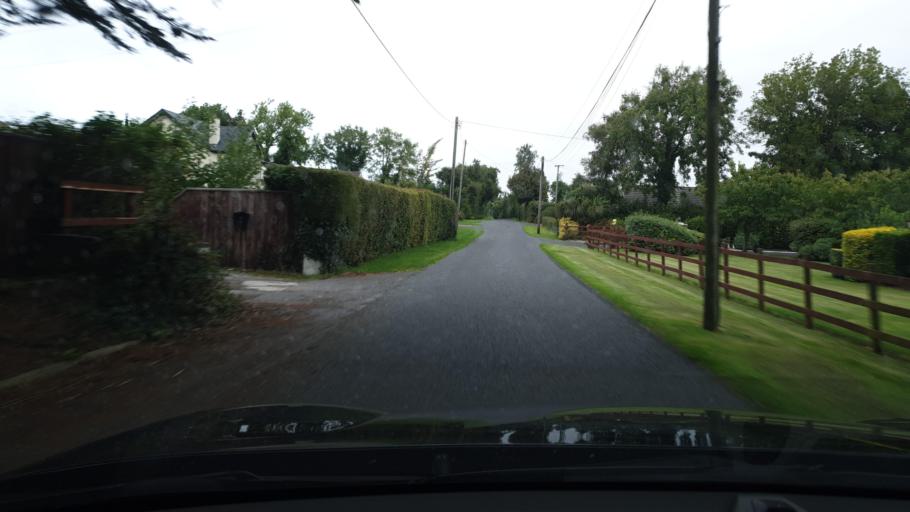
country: IE
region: Leinster
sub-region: An Mhi
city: Ratoath
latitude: 53.5182
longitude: -6.4848
